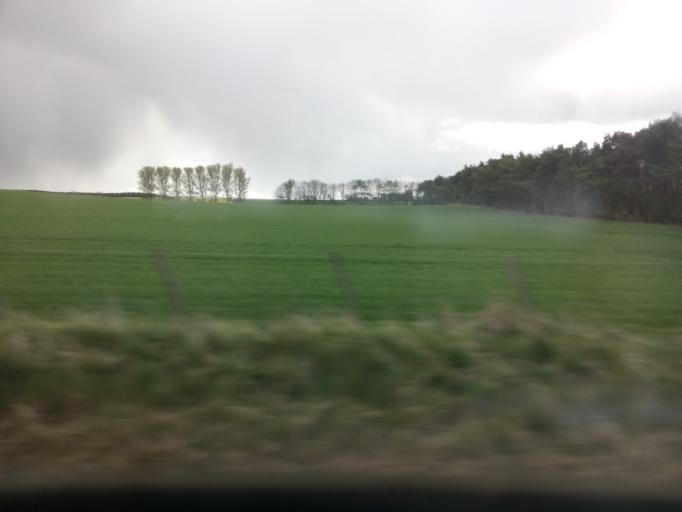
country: GB
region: Scotland
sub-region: East Lothian
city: North Berwick
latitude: 56.0081
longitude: -2.7446
